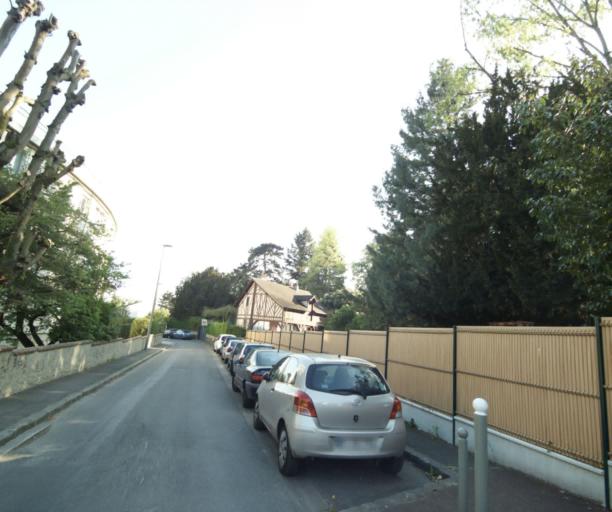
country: FR
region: Ile-de-France
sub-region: Departement des Hauts-de-Seine
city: Ville-d'Avray
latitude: 48.8206
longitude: 2.1943
